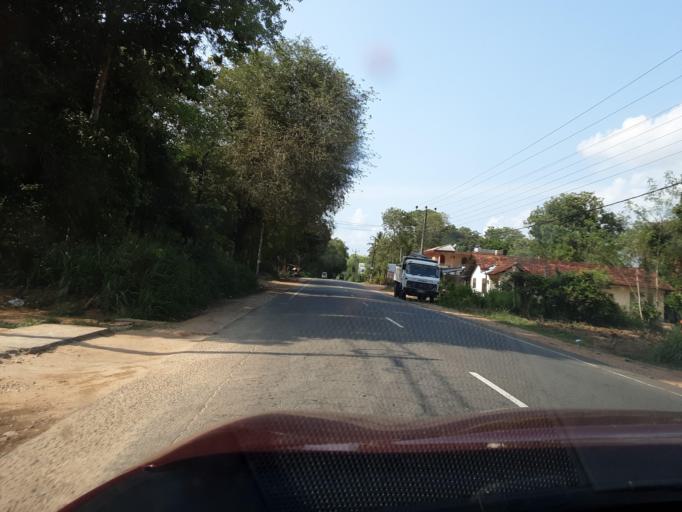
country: LK
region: Uva
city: Haputale
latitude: 6.5852
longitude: 81.1410
